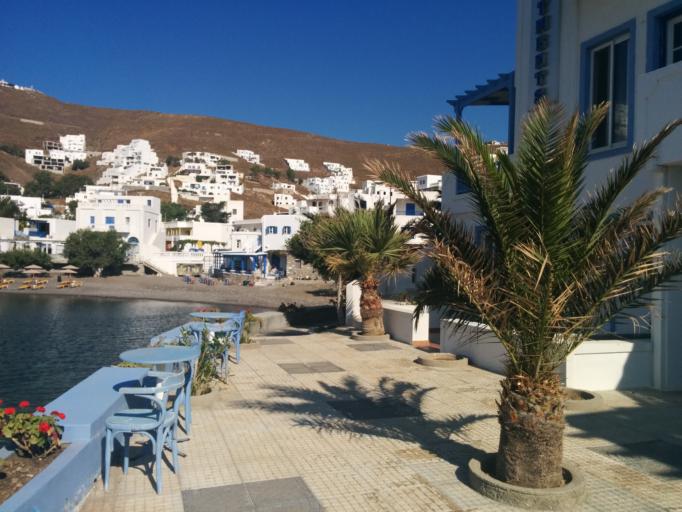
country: GR
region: South Aegean
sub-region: Nomos Dodekanisou
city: Astypalaia
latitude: 36.5490
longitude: 26.3540
